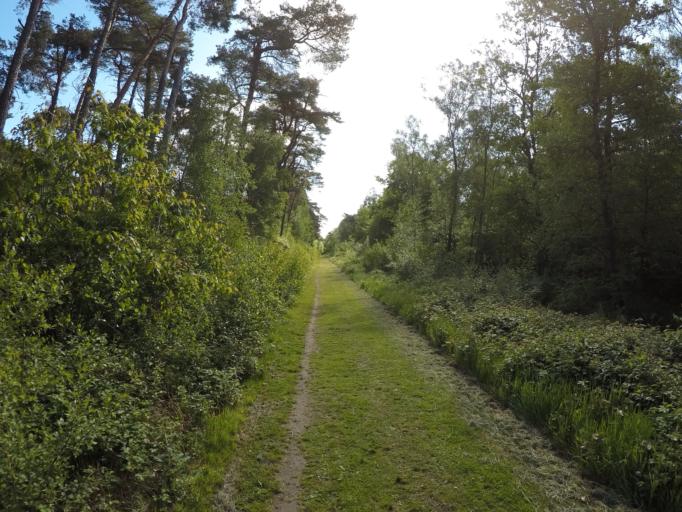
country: BE
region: Flanders
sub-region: Provincie Antwerpen
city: Schoten
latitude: 51.2666
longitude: 4.4903
